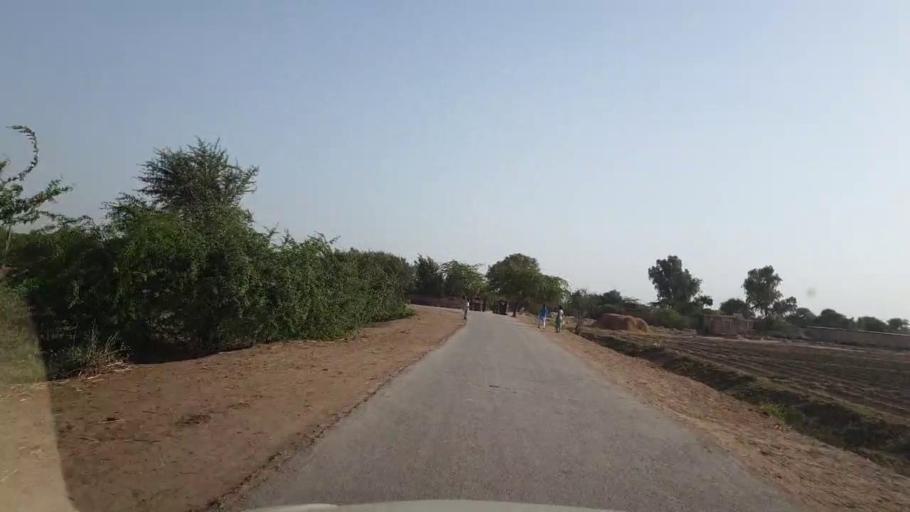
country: PK
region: Sindh
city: Tando Ghulam Ali
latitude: 25.0861
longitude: 68.8689
